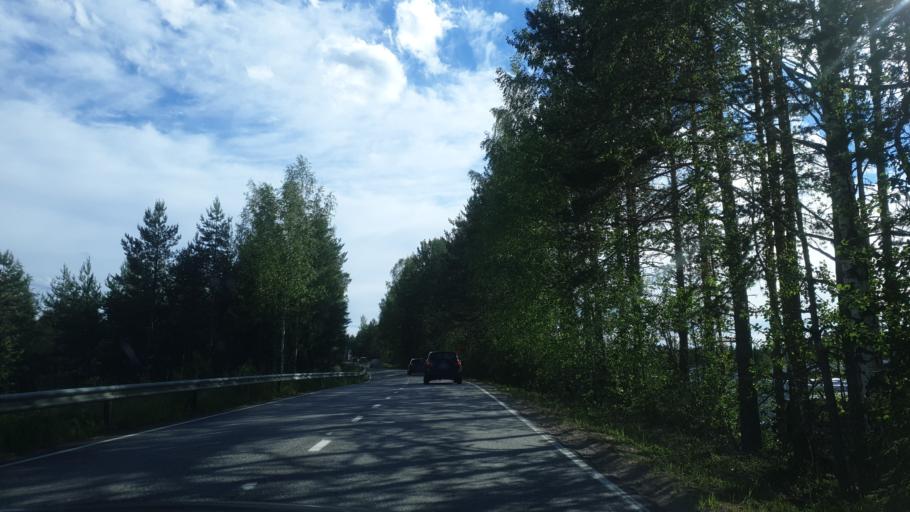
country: FI
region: Southern Savonia
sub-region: Mikkeli
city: Pertunmaa
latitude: 61.4878
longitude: 26.4696
